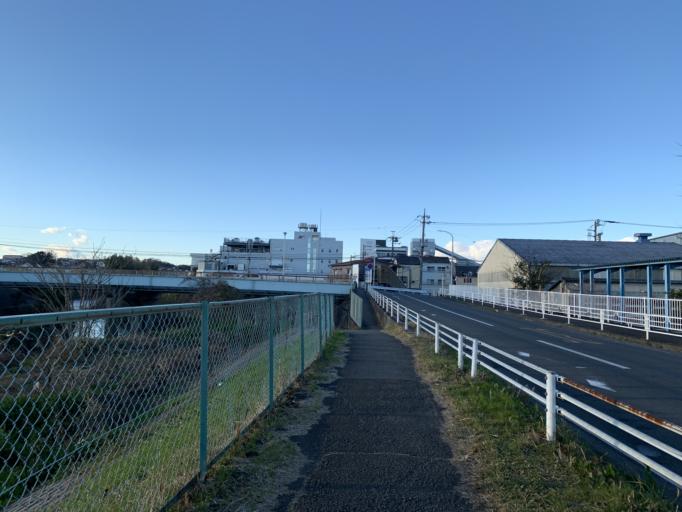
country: JP
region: Tokyo
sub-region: Machida-shi
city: Machida
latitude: 35.5183
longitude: 139.5518
